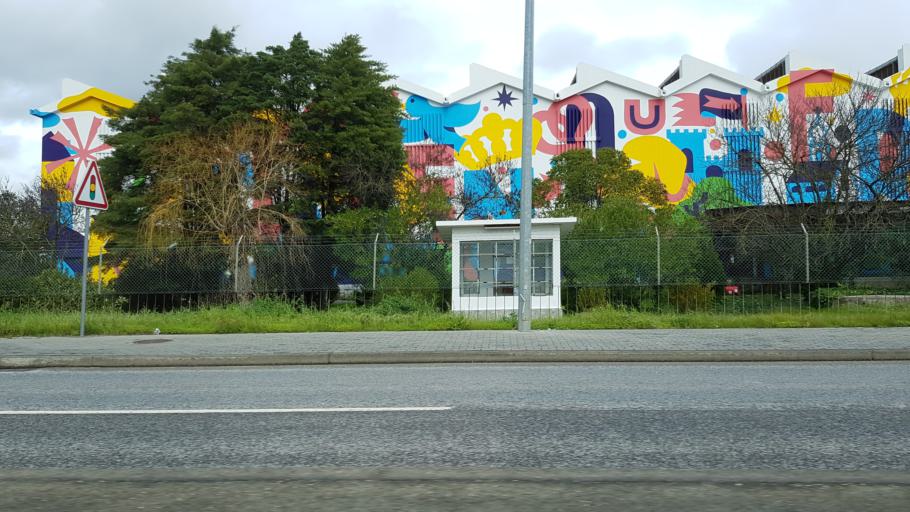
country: PT
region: Lisbon
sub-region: Alenquer
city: Carregado
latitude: 39.0383
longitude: -8.9850
